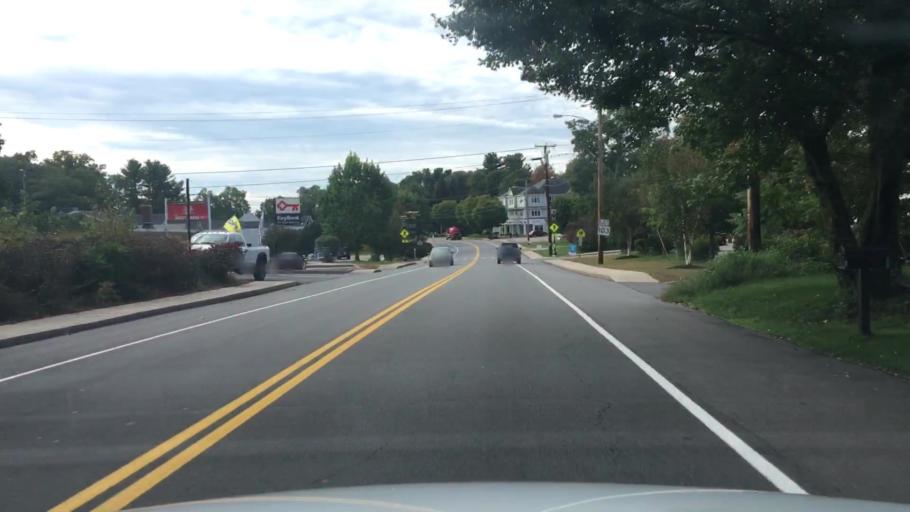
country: US
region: Maine
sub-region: York County
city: Kittery
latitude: 43.0911
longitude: -70.7370
